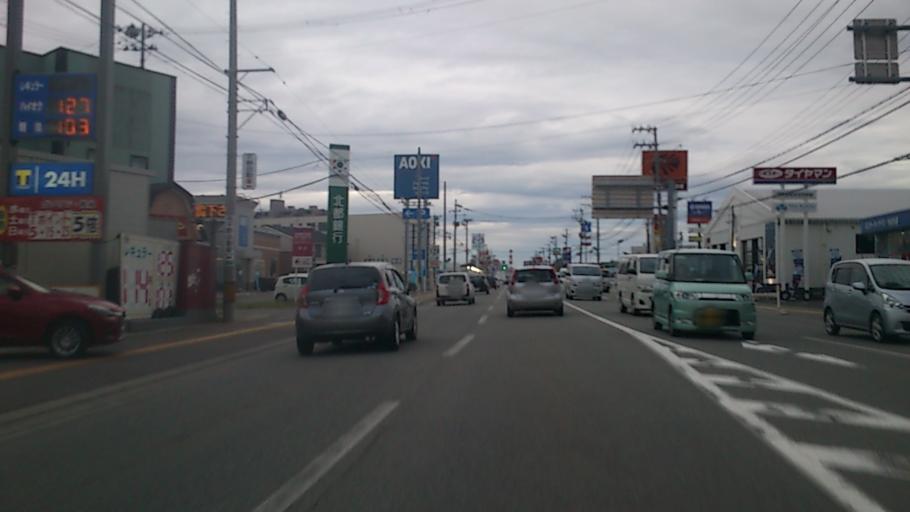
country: JP
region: Akita
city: Akita Shi
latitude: 39.7363
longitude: 140.0984
